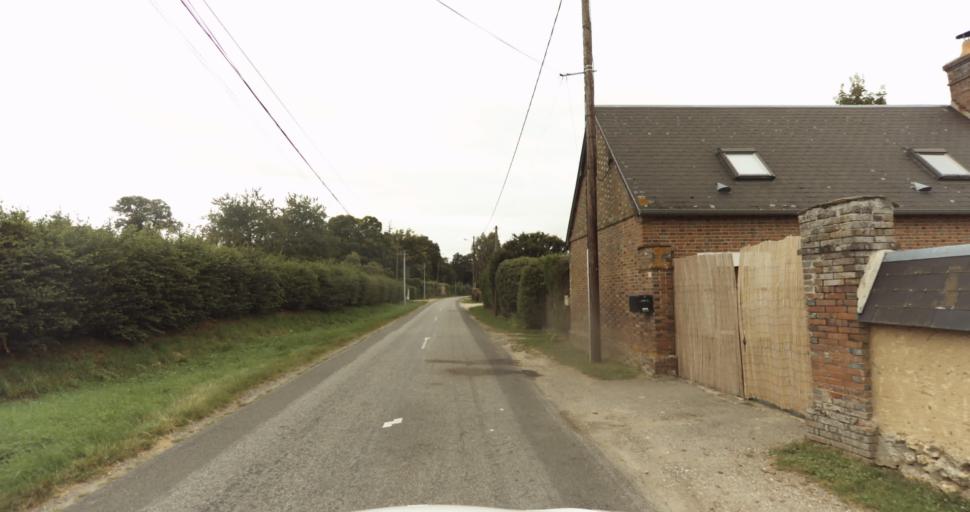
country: FR
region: Haute-Normandie
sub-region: Departement de l'Eure
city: Arnieres-sur-Iton
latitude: 48.9543
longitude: 1.0674
